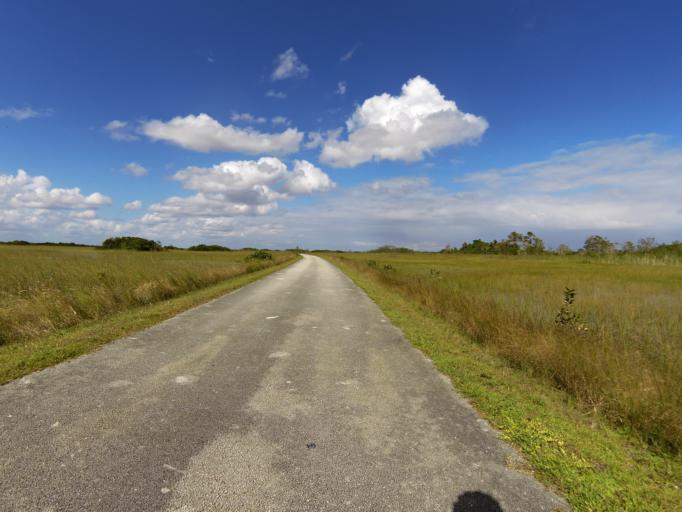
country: US
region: Florida
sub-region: Miami-Dade County
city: The Hammocks
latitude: 25.7244
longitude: -80.7590
